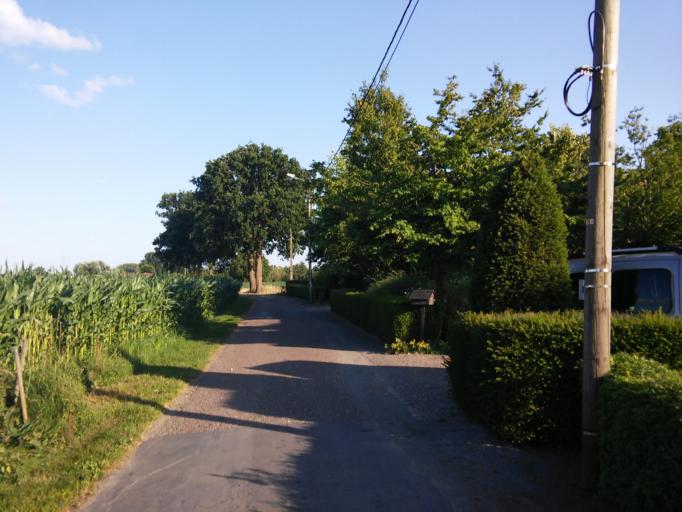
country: BE
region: Flanders
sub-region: Provincie Antwerpen
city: Rumst
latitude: 51.0520
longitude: 4.3987
